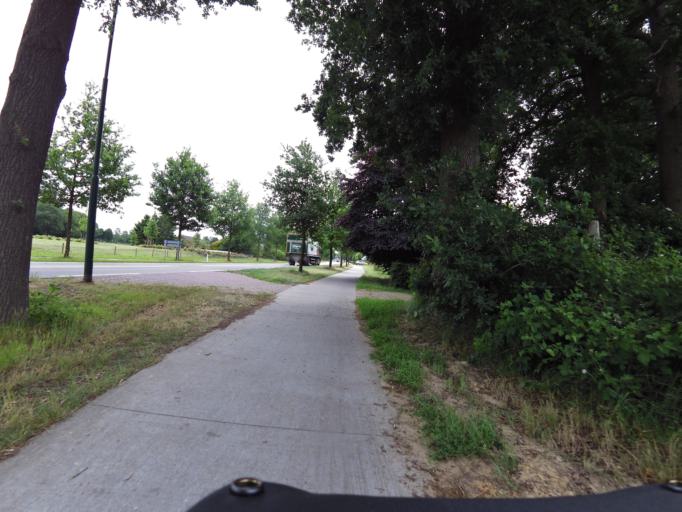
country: NL
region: North Brabant
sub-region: Gemeente Hilvarenbeek
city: Hilvarenbeek
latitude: 51.4807
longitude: 5.1614
